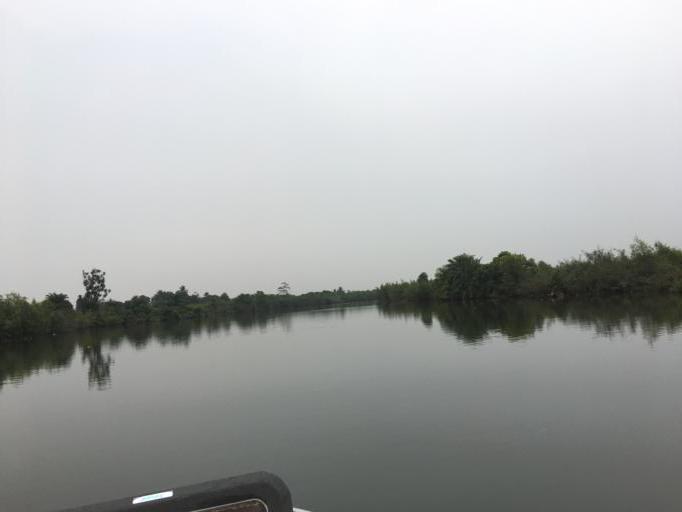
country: LR
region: Montserrado
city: Monrovia
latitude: 6.3665
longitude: -10.7747
